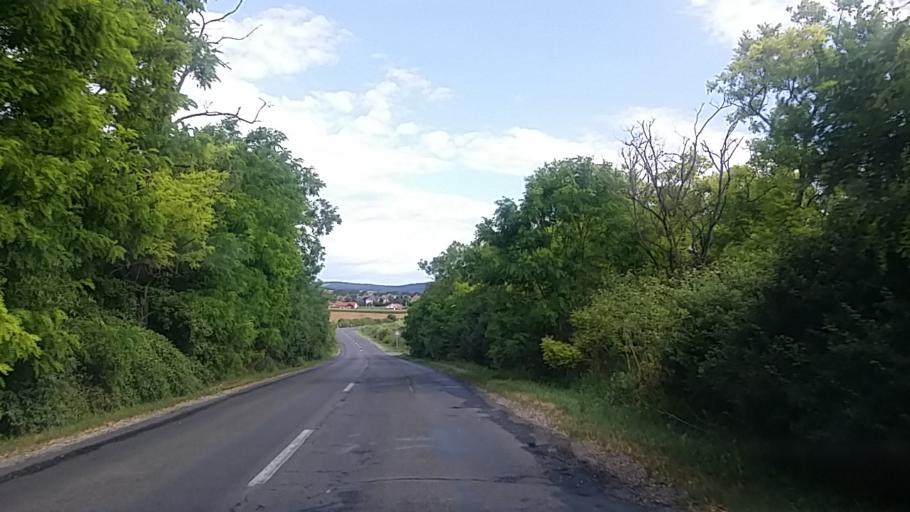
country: HU
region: Pest
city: Kosd
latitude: 47.7769
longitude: 19.2184
